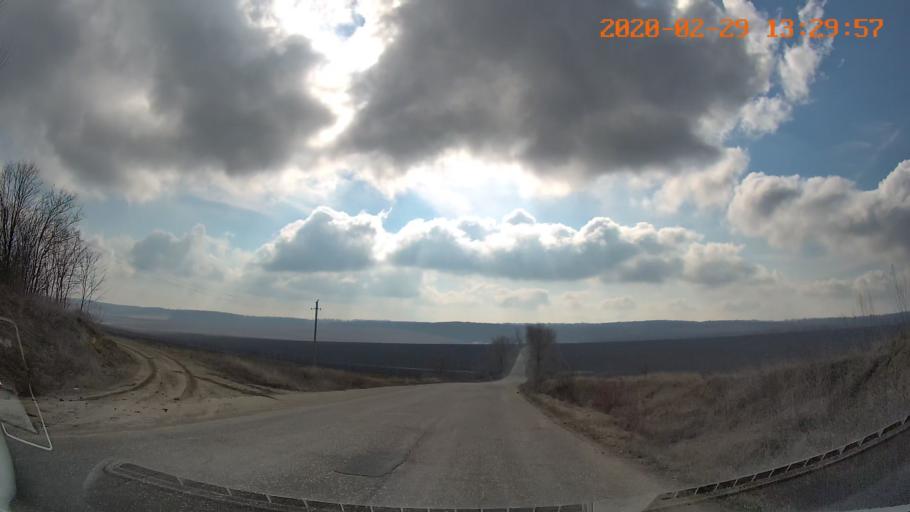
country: MD
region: Telenesti
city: Camenca
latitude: 47.8918
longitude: 28.6327
